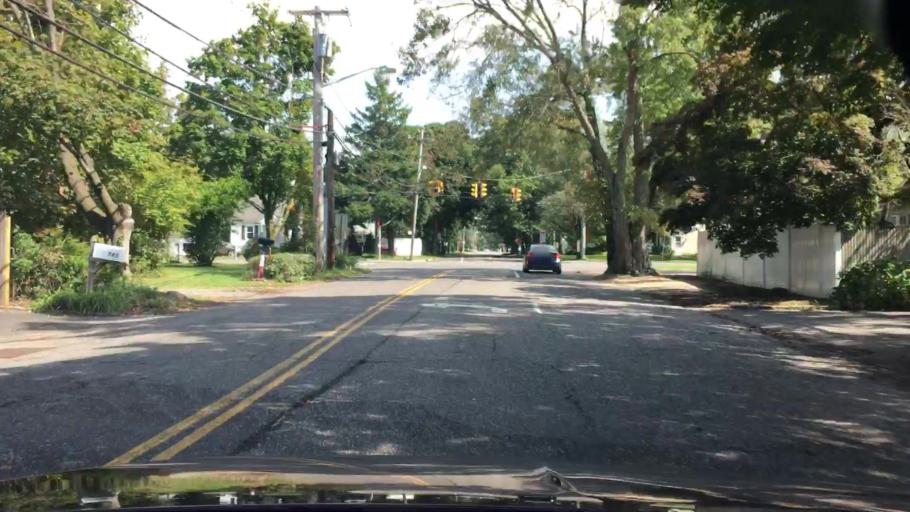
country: US
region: New York
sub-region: Suffolk County
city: Ronkonkoma
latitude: 40.8008
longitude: -73.1241
